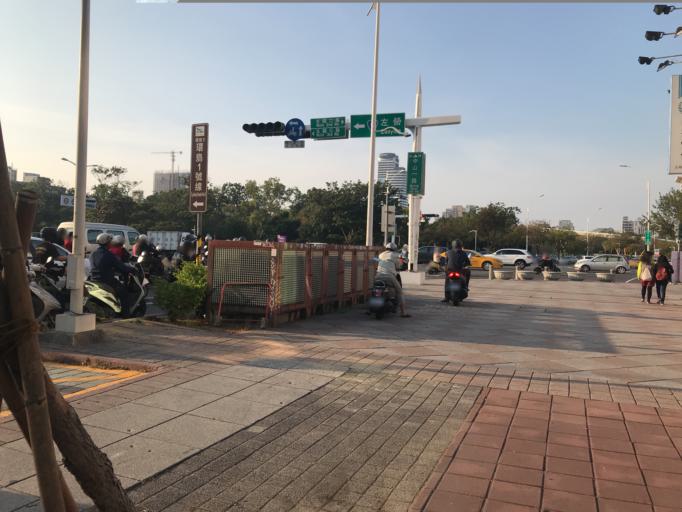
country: TW
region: Kaohsiung
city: Kaohsiung
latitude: 22.6228
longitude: 120.3013
